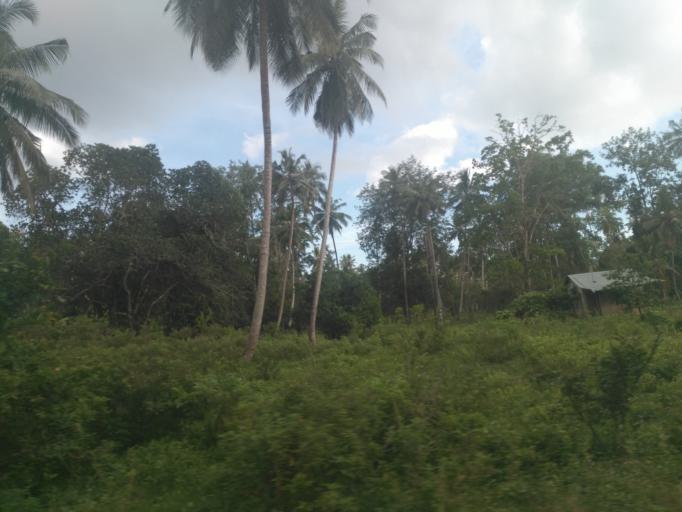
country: TZ
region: Zanzibar Central/South
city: Koani
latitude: -6.1067
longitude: 39.2920
